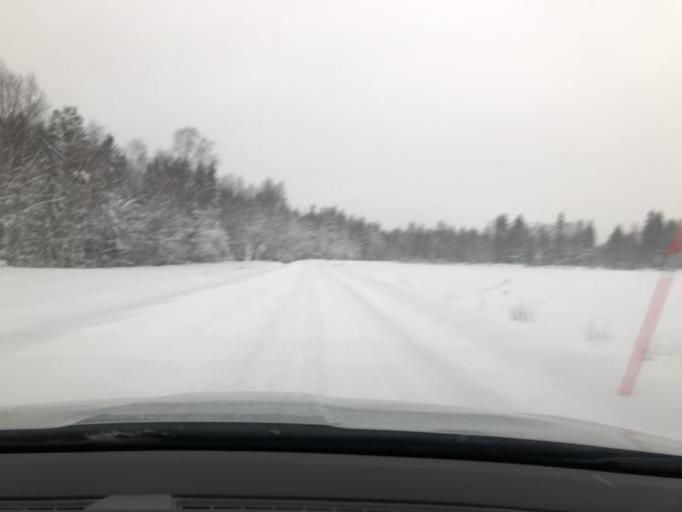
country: SE
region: Vaesterbotten
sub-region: Umea Kommun
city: Saevar
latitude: 63.9422
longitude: 20.7107
